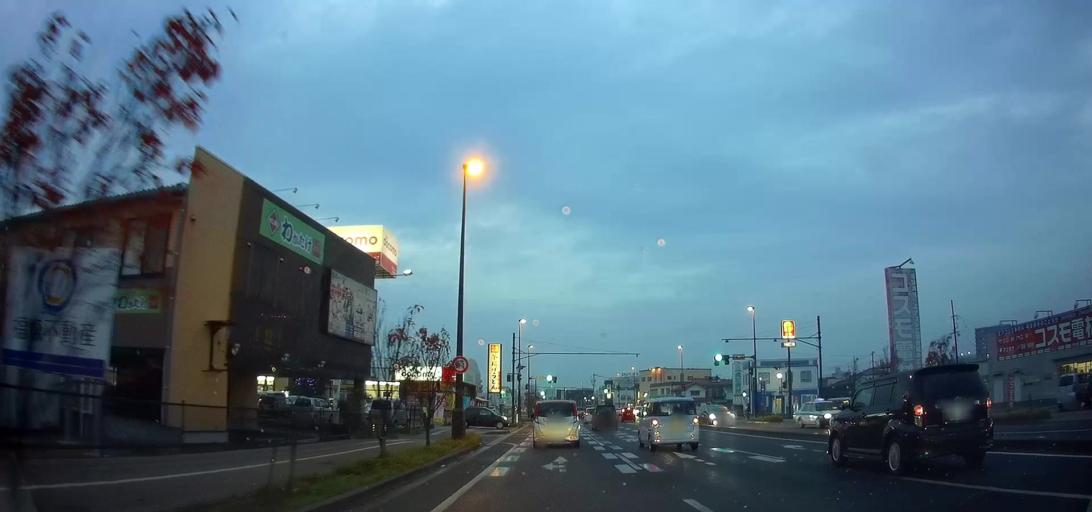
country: JP
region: Nagasaki
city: Omura
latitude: 32.9044
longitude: 129.9575
